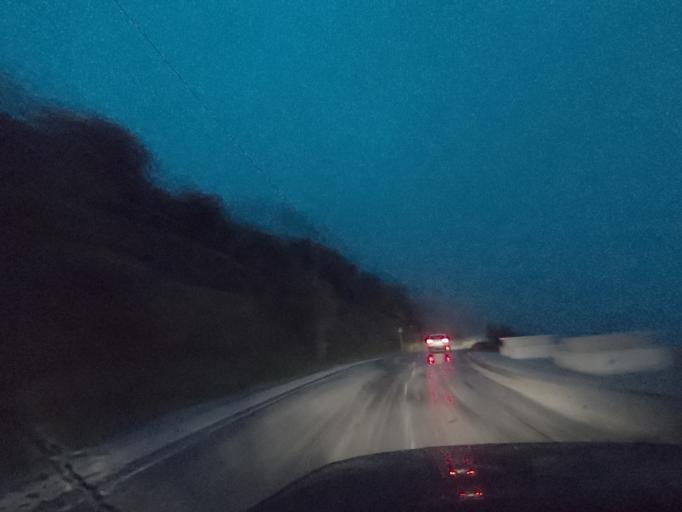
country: PT
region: Vila Real
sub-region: Sabrosa
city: Vilela
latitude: 41.2083
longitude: -7.5546
